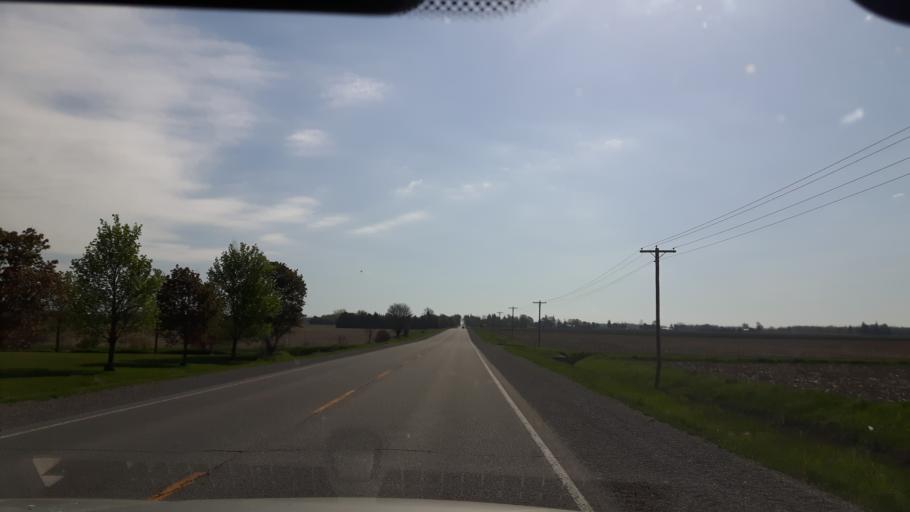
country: CA
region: Ontario
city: Bluewater
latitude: 43.5236
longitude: -81.5353
